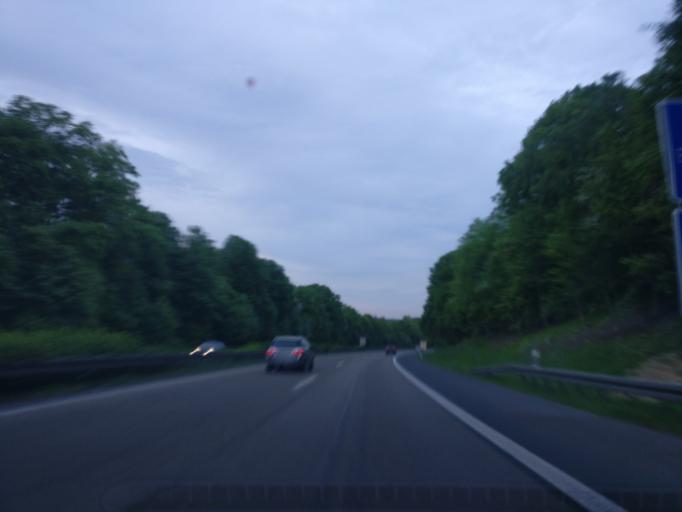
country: DE
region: Hesse
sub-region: Regierungsbezirk Kassel
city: Baunatal
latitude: 51.2346
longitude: 9.4260
